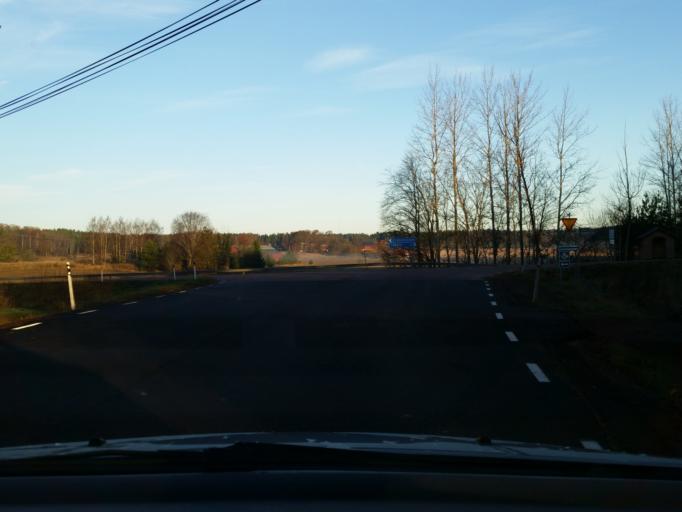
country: AX
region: Alands landsbygd
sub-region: Sund
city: Sund
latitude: 60.2397
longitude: 20.0714
